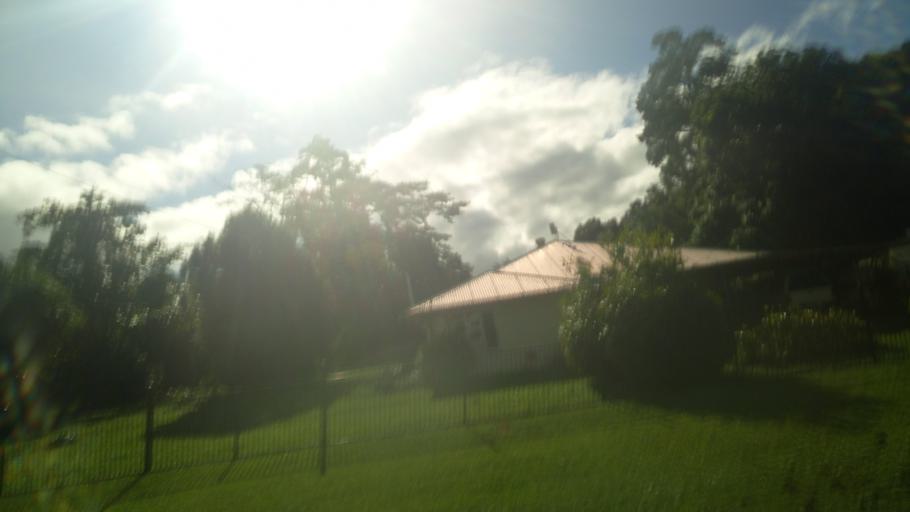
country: AU
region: Queensland
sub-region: Cassowary Coast
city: Innisfail
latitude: -17.5366
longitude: 145.9672
